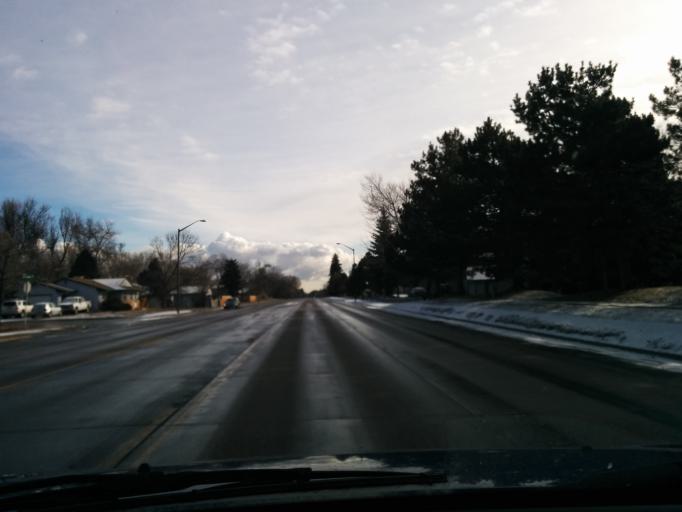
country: US
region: Colorado
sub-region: Larimer County
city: Fort Collins
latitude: 40.5674
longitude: -105.1078
